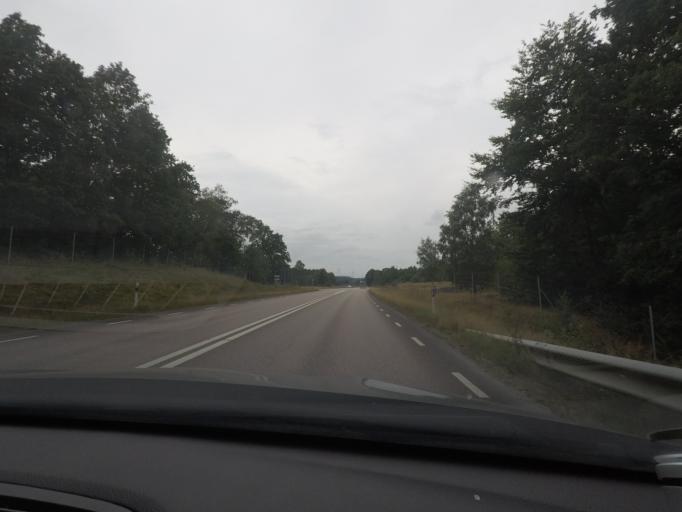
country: SE
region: Halland
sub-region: Laholms Kommun
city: Knared
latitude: 56.5245
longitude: 13.2488
